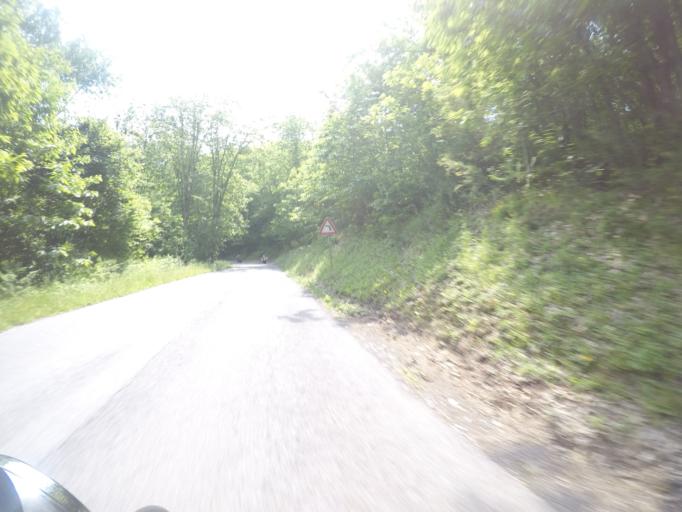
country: IT
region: Tuscany
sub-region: Provincia di Lucca
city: Careggine
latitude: 44.1344
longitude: 10.3457
